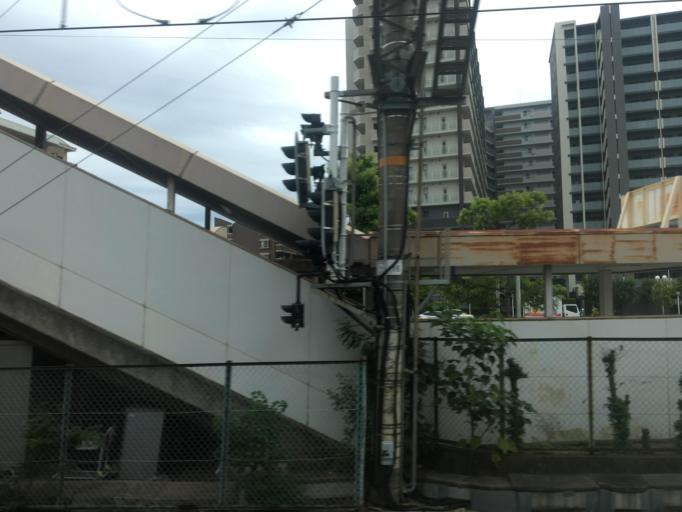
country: JP
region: Osaka
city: Kaizuka
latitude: 34.3902
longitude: 135.3311
